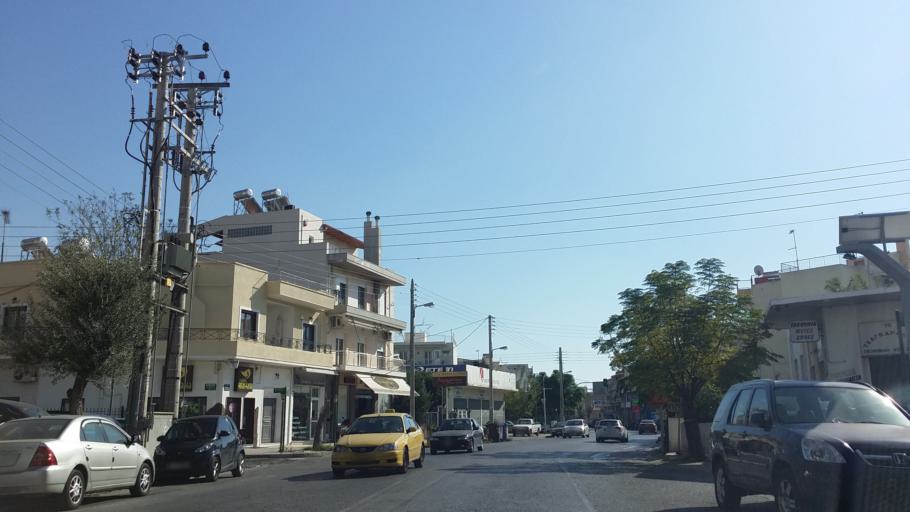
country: GR
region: Attica
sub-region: Nomarchia Athinas
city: Peristeri
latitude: 38.0133
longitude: 23.7090
